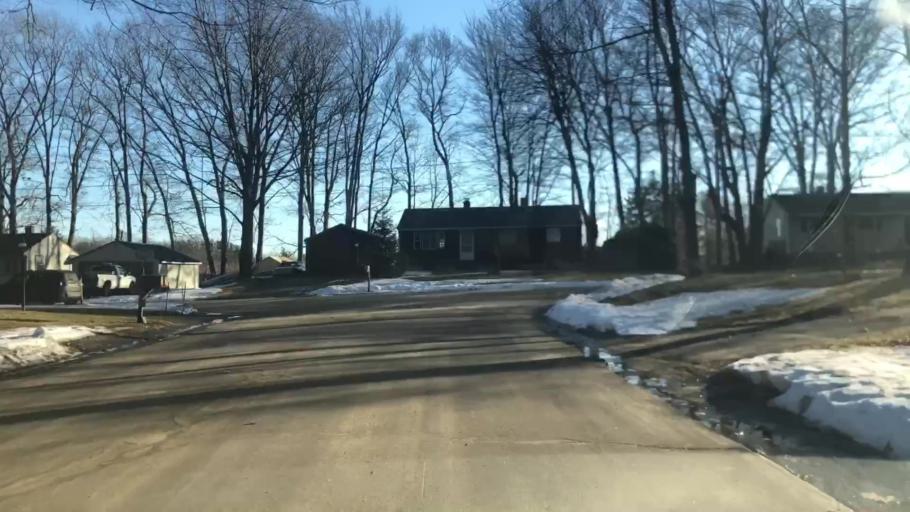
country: US
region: New Hampshire
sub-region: Hillsborough County
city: Milford
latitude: 42.8336
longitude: -71.6680
